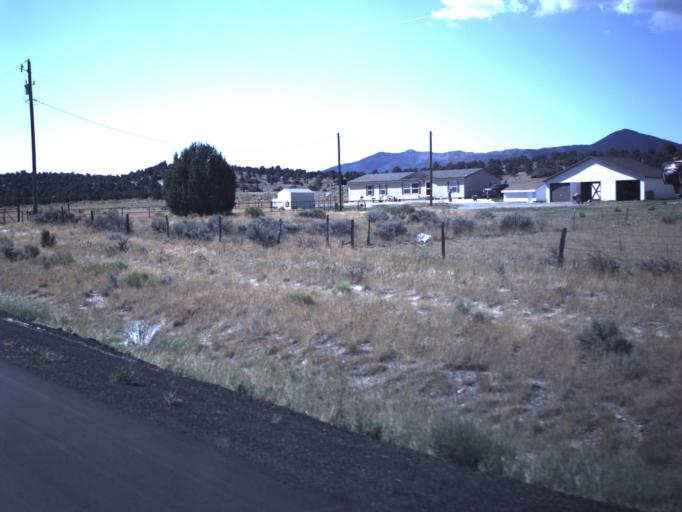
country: US
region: Utah
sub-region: Utah County
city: Eagle Mountain
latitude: 40.0239
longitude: -112.2813
